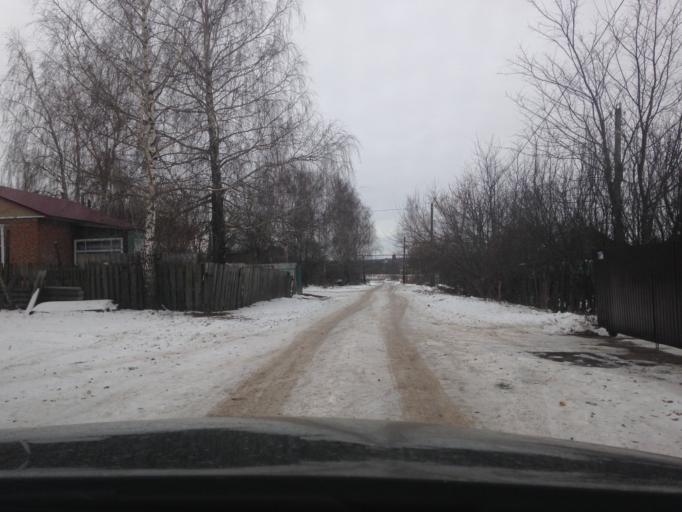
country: RU
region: Tula
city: Priupskiy
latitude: 53.7776
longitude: 37.6525
